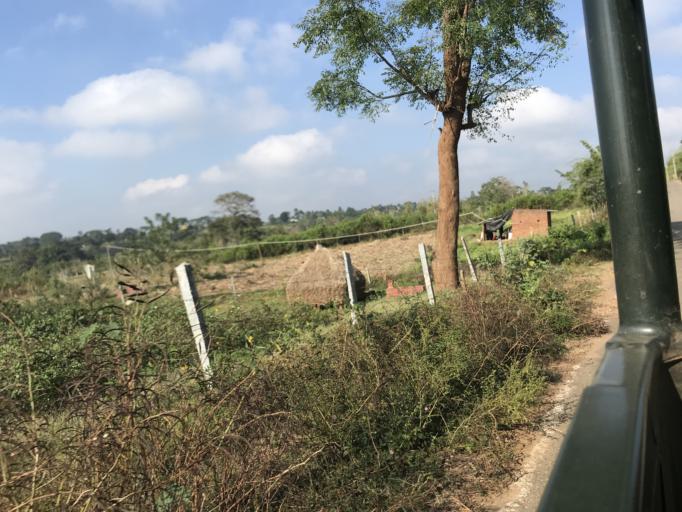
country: IN
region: Karnataka
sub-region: Mysore
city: Heggadadevankote
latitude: 11.9462
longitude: 76.2641
